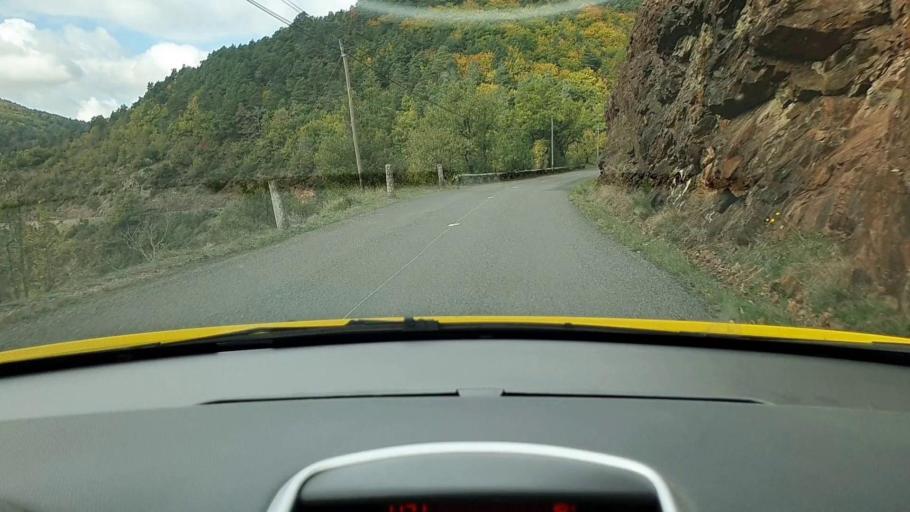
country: FR
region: Languedoc-Roussillon
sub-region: Departement de la Lozere
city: Meyrueis
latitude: 44.1129
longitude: 3.4366
